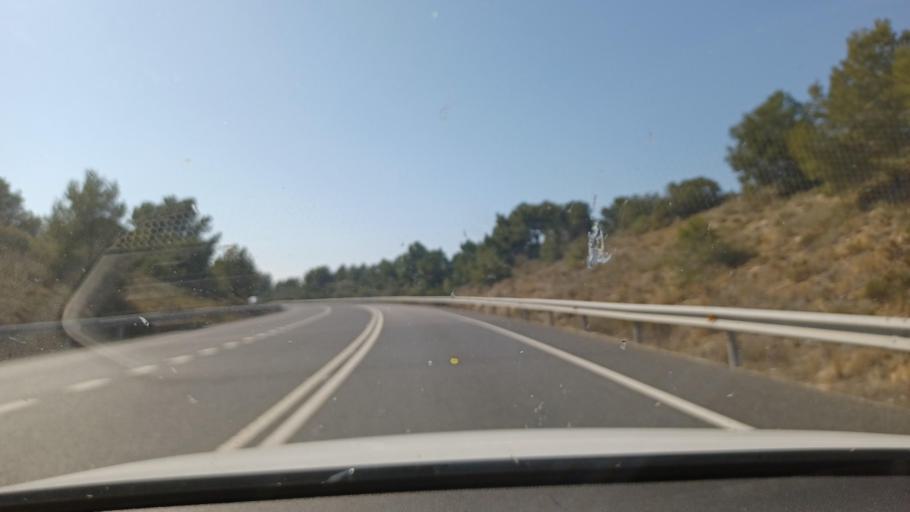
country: ES
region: Catalonia
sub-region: Provincia de Tarragona
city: El Perello
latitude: 40.8604
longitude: 0.7170
